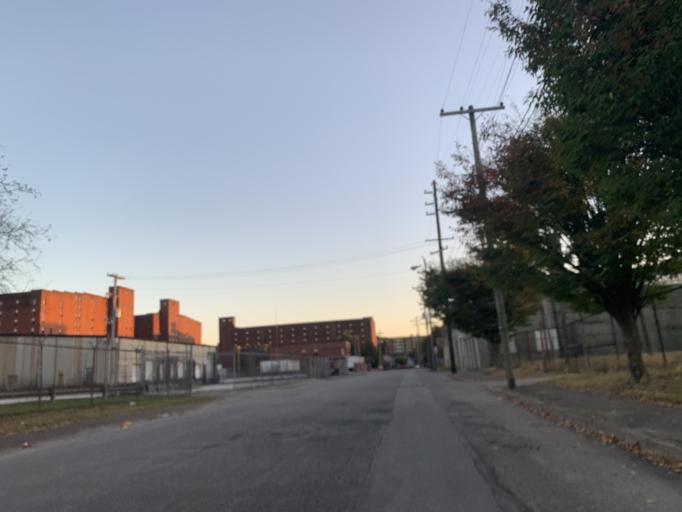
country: US
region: Kentucky
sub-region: Jefferson County
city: Louisville
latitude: 38.2463
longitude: -85.7804
